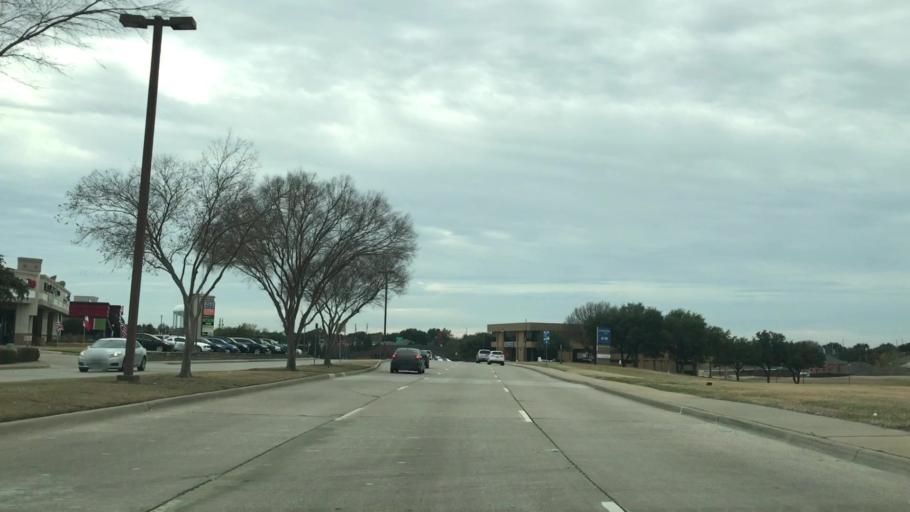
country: US
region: Texas
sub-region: Dallas County
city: Carrollton
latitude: 32.9888
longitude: -96.8903
